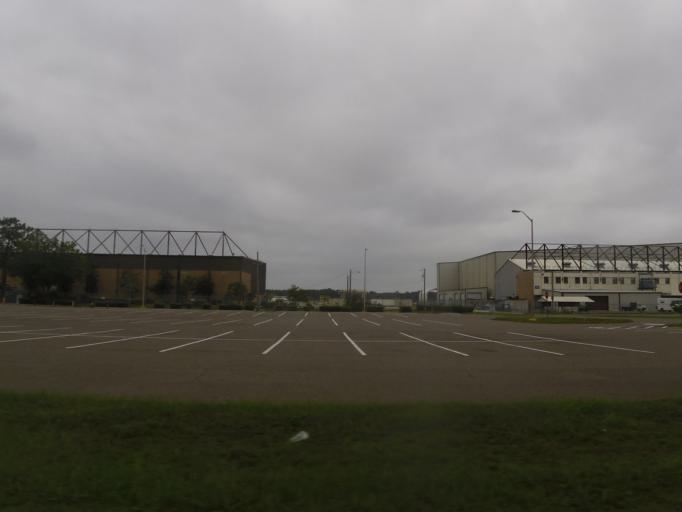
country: US
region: Florida
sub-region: Duval County
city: Baldwin
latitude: 30.2331
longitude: -81.8823
